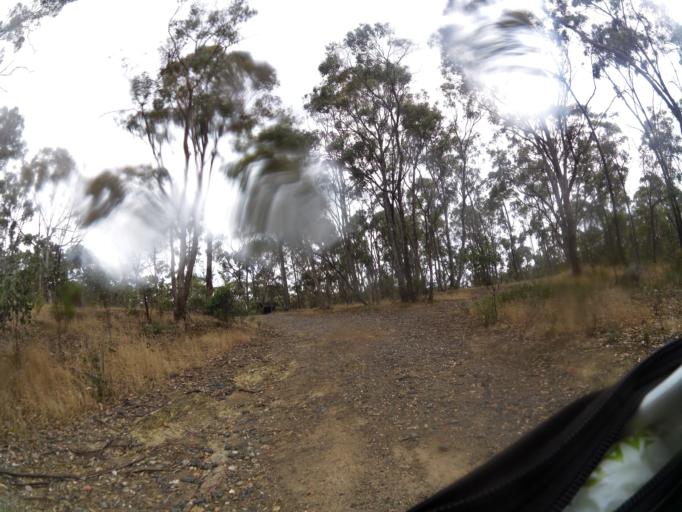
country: AU
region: Victoria
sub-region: Mount Alexander
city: Castlemaine
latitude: -37.0716
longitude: 144.2589
